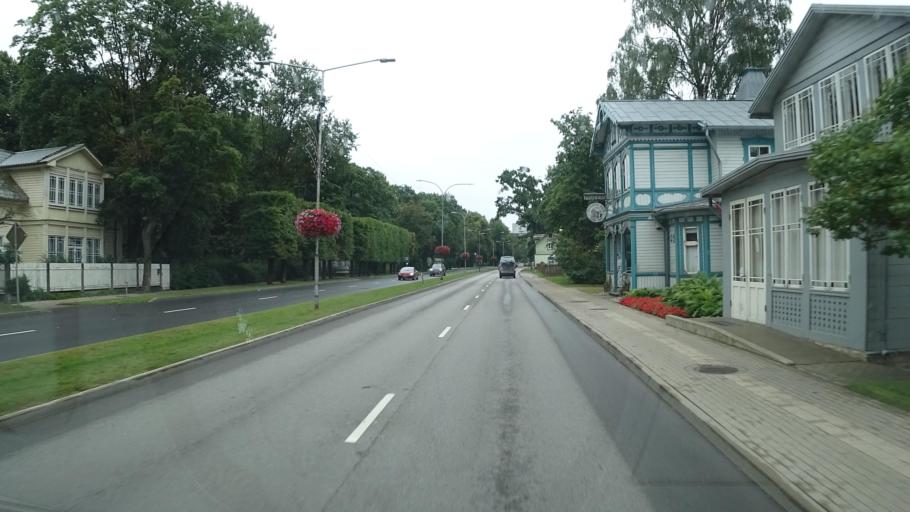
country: LV
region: Jurmala
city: Jurmala
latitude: 56.9703
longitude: 23.7805
